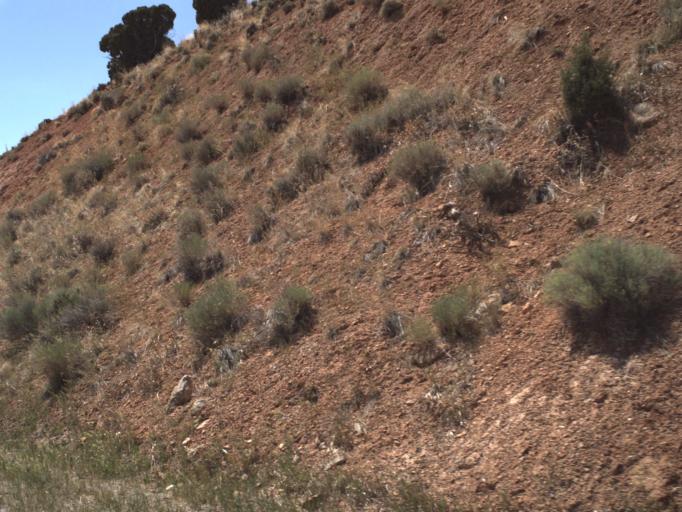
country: US
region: Utah
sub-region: Rich County
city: Randolph
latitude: 41.5021
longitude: -111.2476
